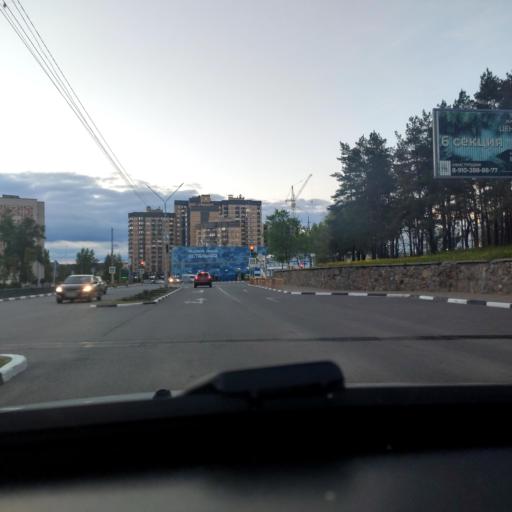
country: RU
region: Voronezj
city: Novovoronezh
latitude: 51.3159
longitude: 39.2073
